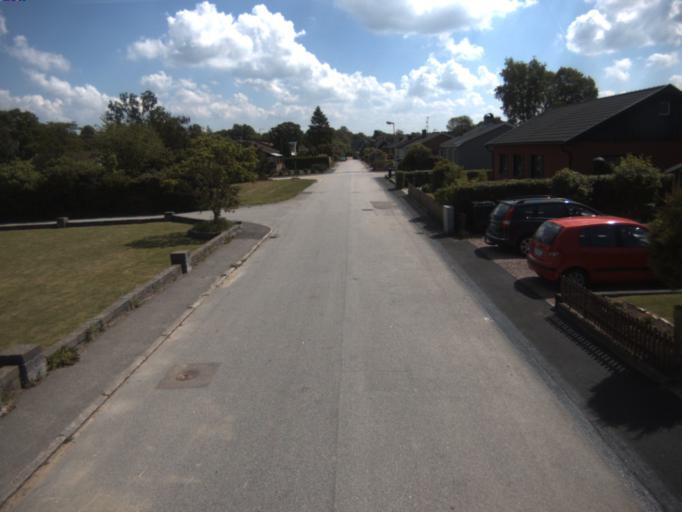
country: SE
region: Skane
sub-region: Helsingborg
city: Barslov
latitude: 56.0321
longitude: 12.8157
